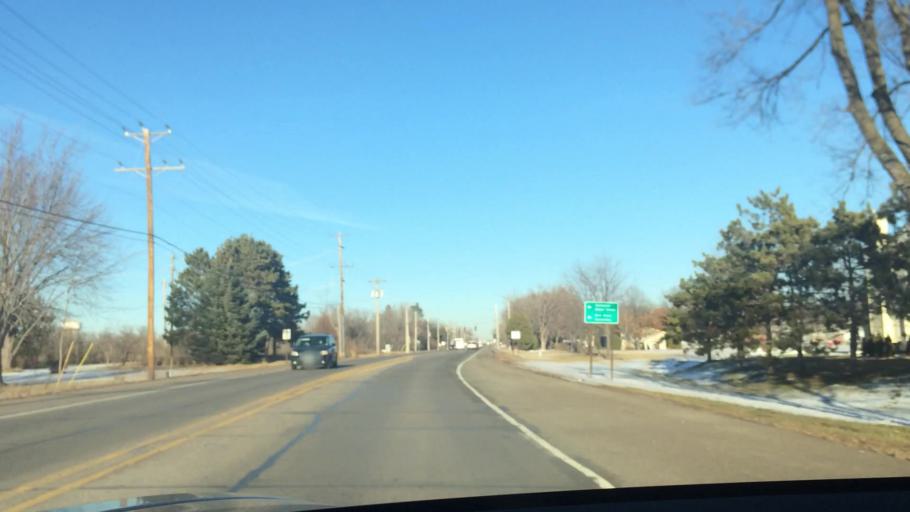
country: US
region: Minnesota
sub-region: Anoka County
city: Lino Lakes
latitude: 45.1666
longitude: -93.1219
